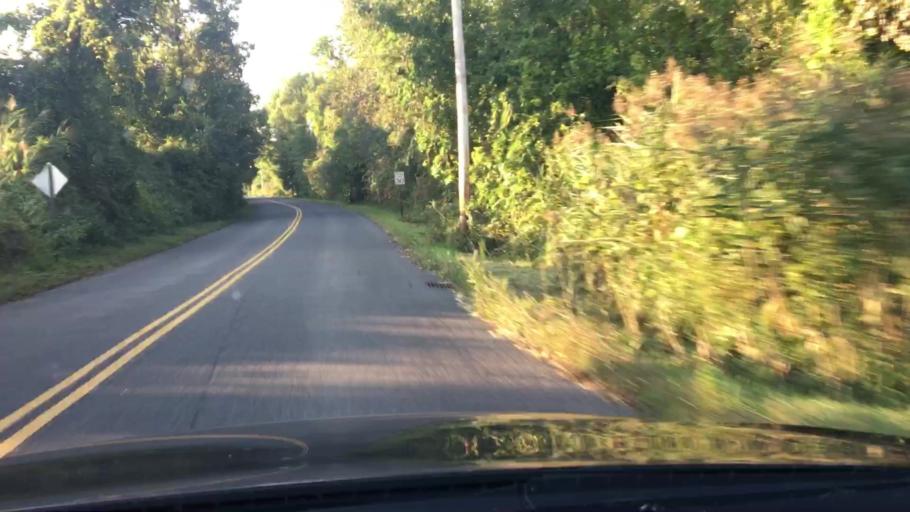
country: US
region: Connecticut
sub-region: Litchfield County
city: New Milford
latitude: 41.6031
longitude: -73.3706
